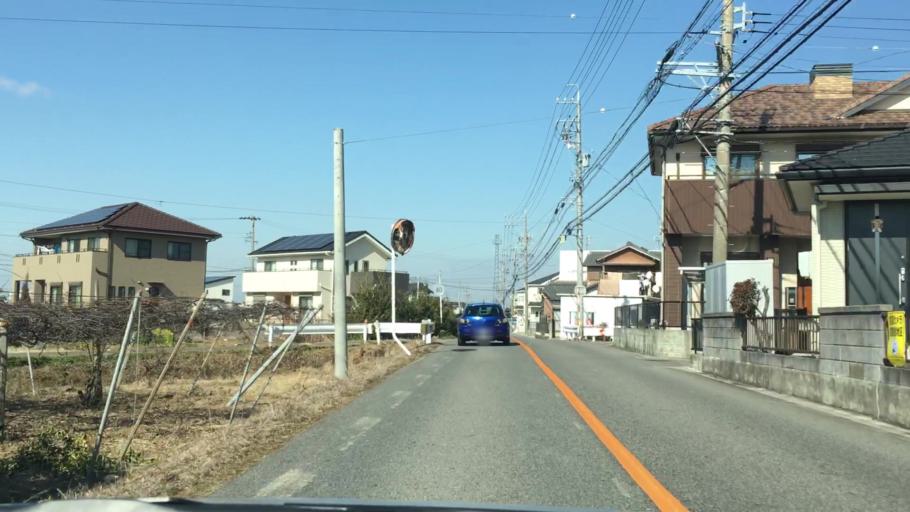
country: JP
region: Aichi
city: Anjo
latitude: 34.9883
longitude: 137.1168
